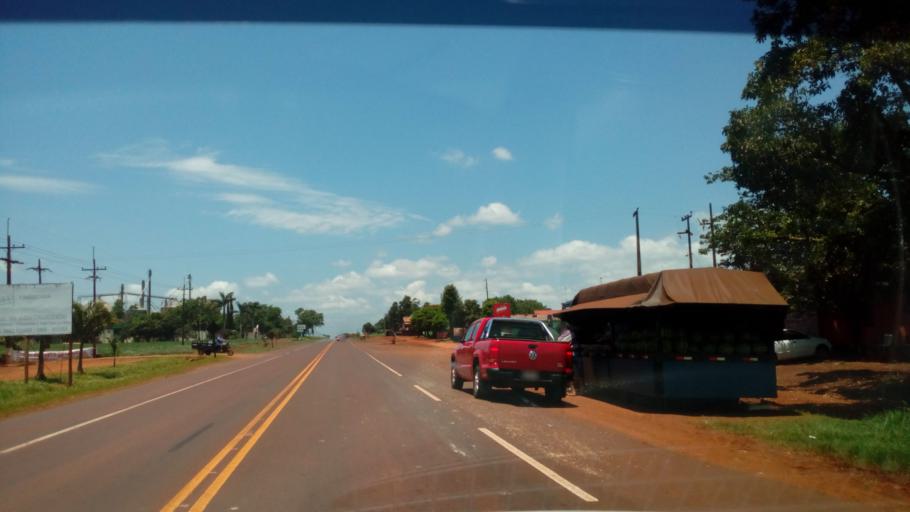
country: PY
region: Alto Parana
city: Naranjal
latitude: -25.9325
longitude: -55.1162
